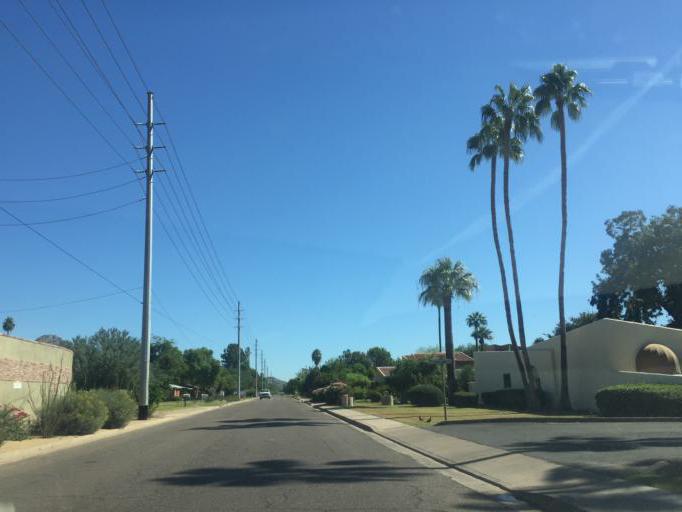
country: US
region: Arizona
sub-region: Maricopa County
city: Phoenix
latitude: 33.5347
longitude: -112.0626
